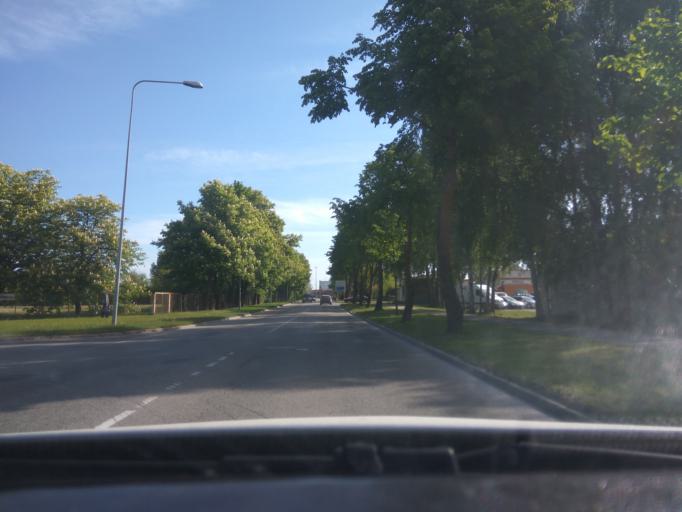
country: LV
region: Ventspils
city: Ventspils
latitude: 57.3829
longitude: 21.5830
